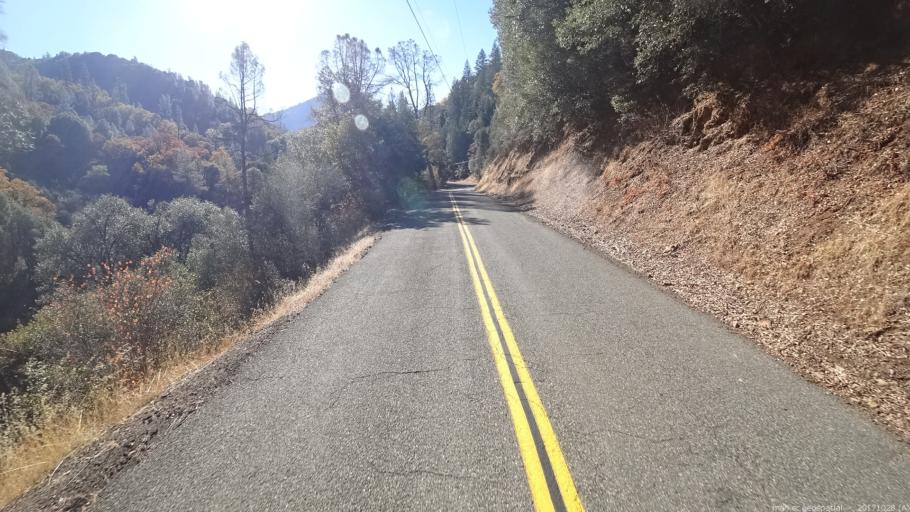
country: US
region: California
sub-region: Trinity County
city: Lewiston
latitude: 40.7724
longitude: -122.6113
